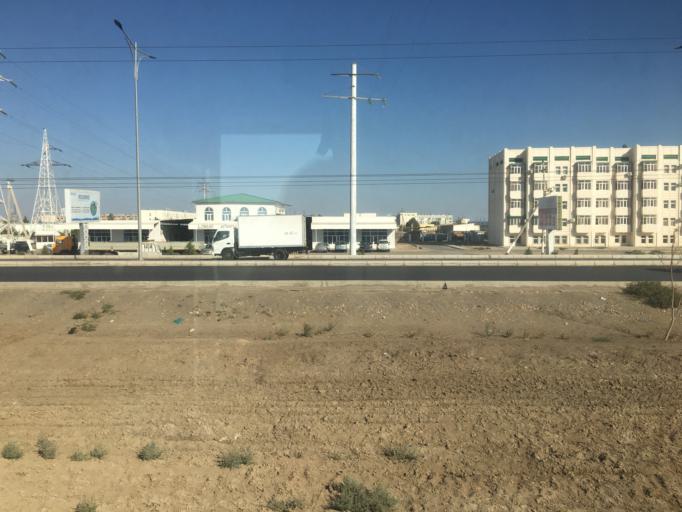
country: TM
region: Lebap
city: Turkmenabat
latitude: 39.0433
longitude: 63.5728
